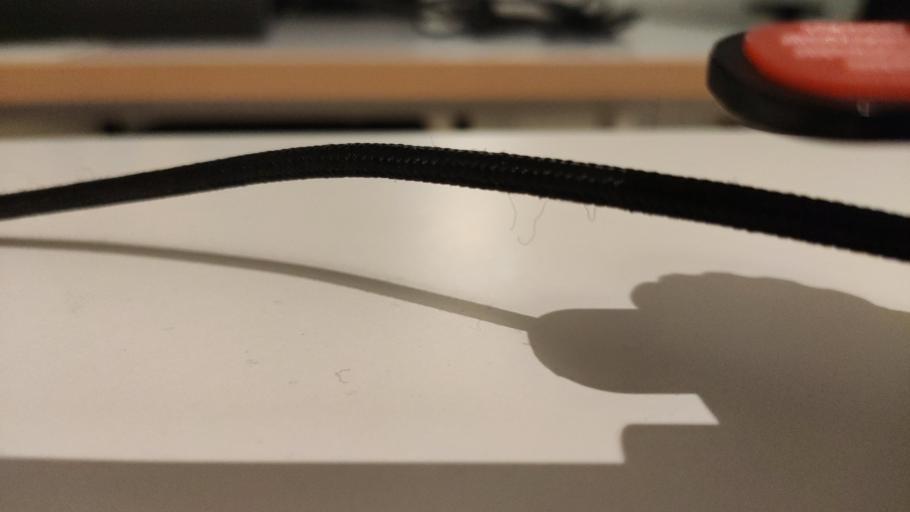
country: RU
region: Moskovskaya
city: Rogachevo
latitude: 56.4324
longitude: 37.1807
